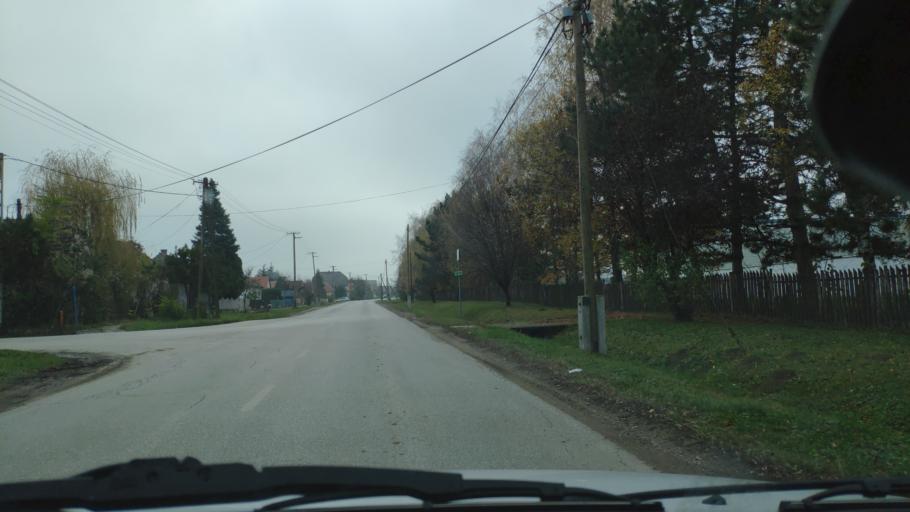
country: HU
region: Somogy
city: Balatonbereny
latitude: 46.6728
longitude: 17.2899
